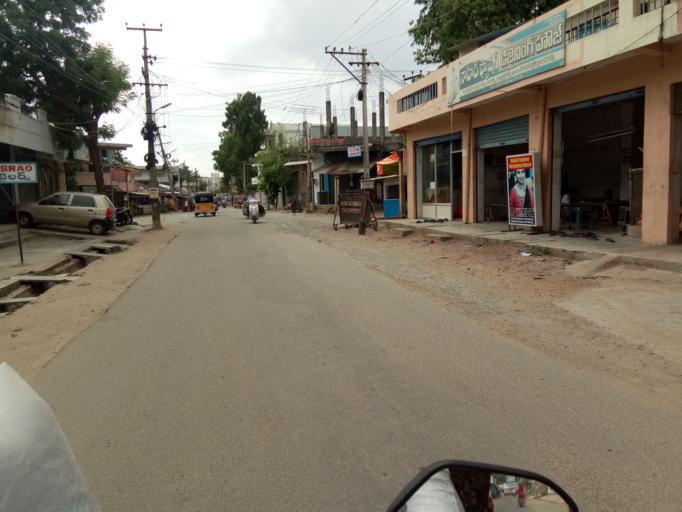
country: IN
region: Telangana
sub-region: Khammam
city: Khammam
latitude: 17.2388
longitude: 80.1447
